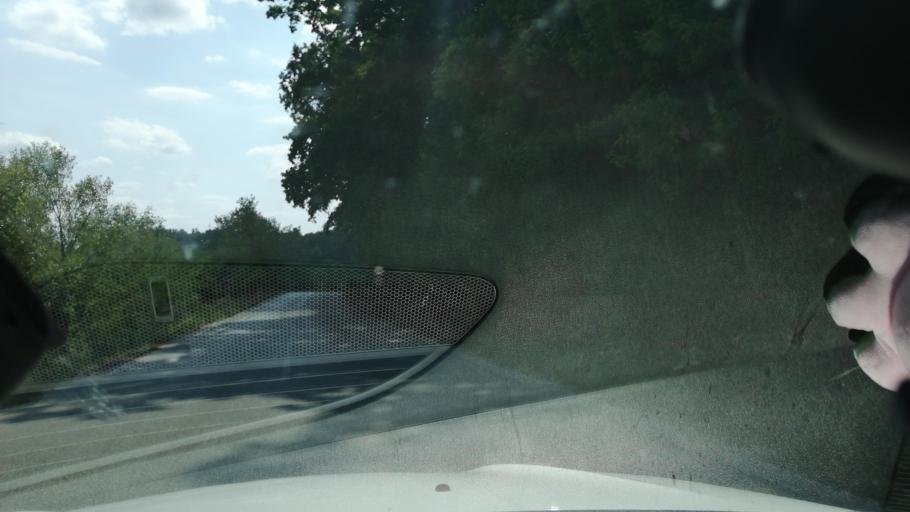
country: RS
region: Central Serbia
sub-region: Moravicki Okrug
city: Cacak
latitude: 43.8018
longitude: 20.2660
